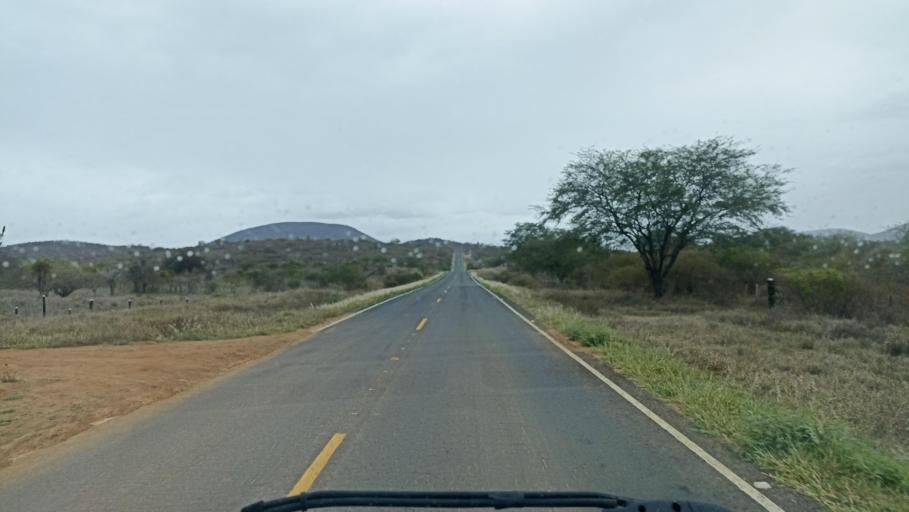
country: BR
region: Bahia
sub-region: Andarai
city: Vera Cruz
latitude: -13.0477
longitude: -40.7612
